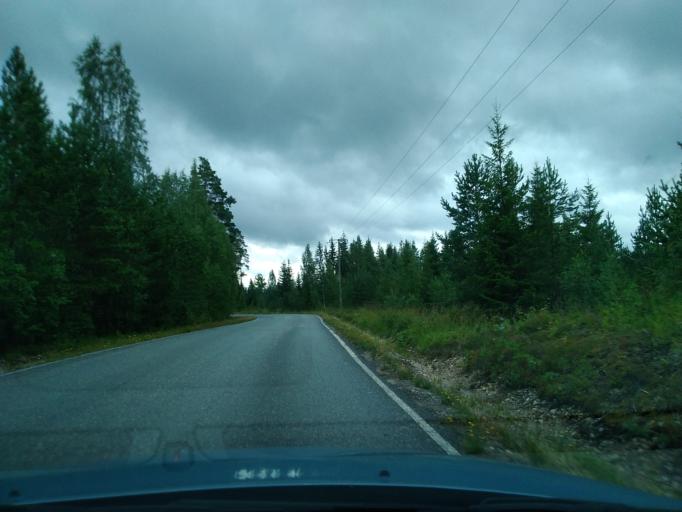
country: FI
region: Uusimaa
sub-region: Helsinki
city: Kaerkoelae
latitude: 60.7482
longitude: 24.0626
